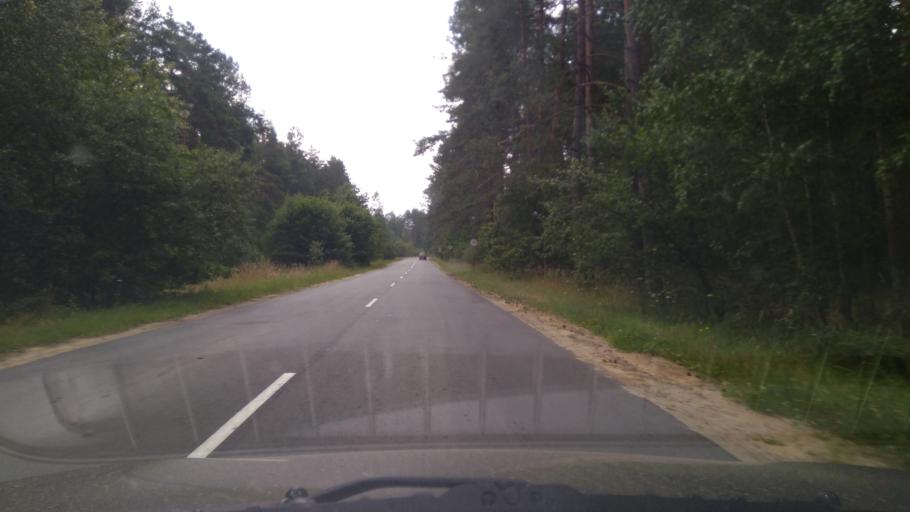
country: BY
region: Brest
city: Nyakhachava
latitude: 52.5963
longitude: 25.1032
